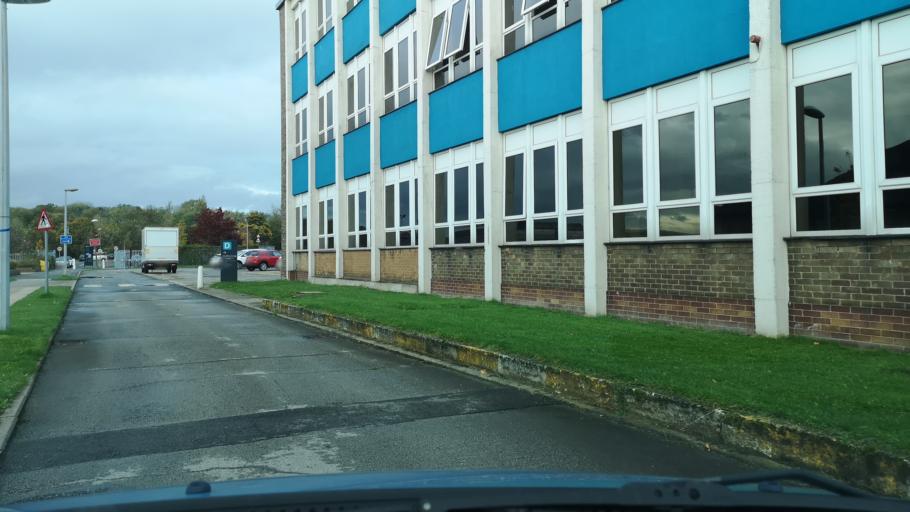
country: GB
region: England
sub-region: North Lincolnshire
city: Scunthorpe
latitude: 53.5781
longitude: -0.6676
